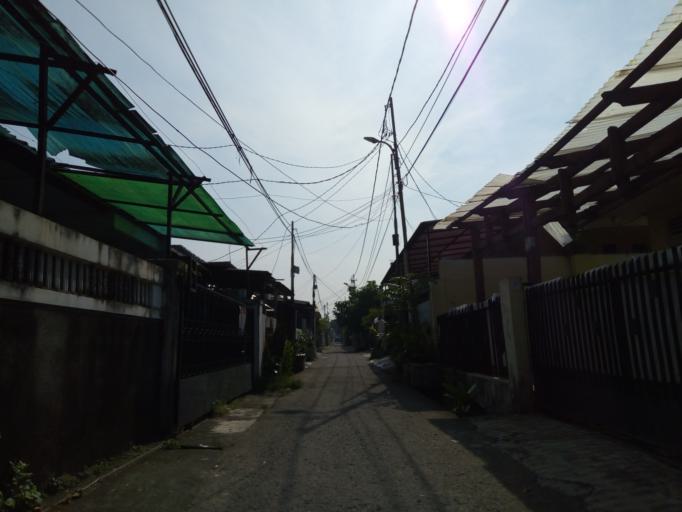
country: ID
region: Jakarta Raya
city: Jakarta
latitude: -6.2109
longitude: 106.8358
